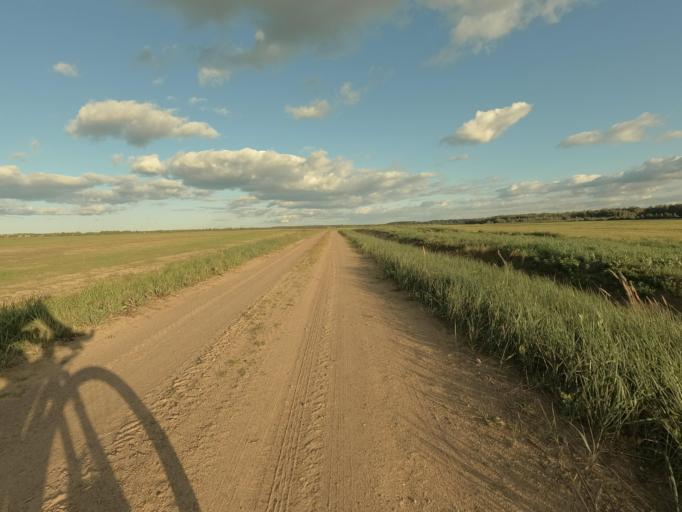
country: RU
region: Leningrad
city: Imeni Sverdlova
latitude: 59.8629
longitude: 30.7444
